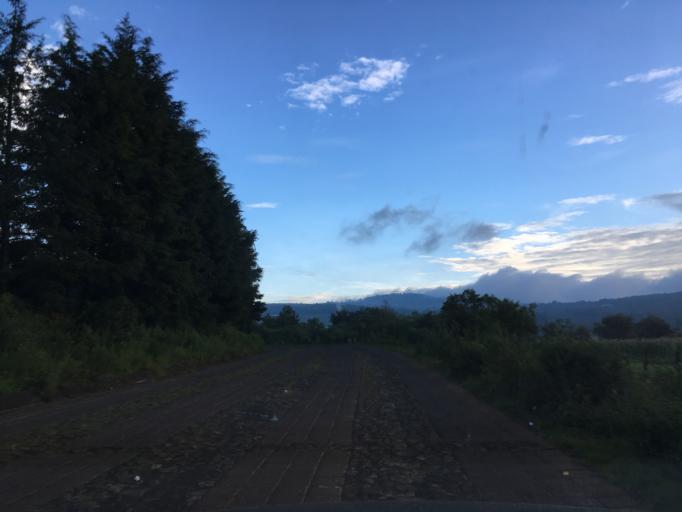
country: MX
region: Michoacan
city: Villa Escalante
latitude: 19.4292
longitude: -101.7145
